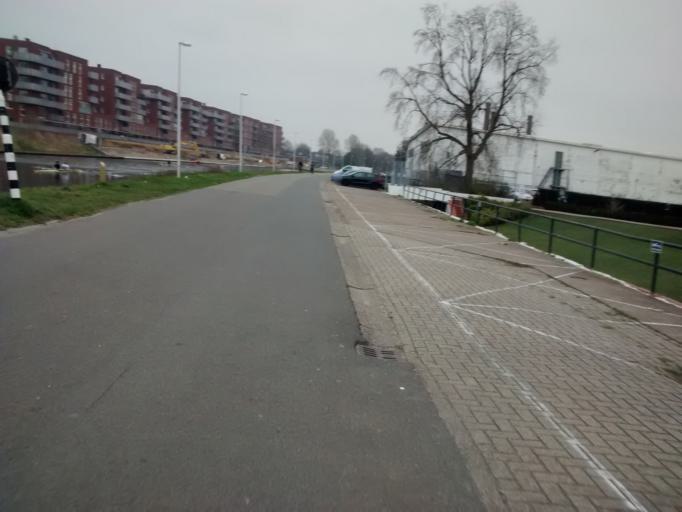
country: NL
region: Utrecht
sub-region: Gemeente Utrecht
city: Utrecht
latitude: 52.0815
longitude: 5.1051
